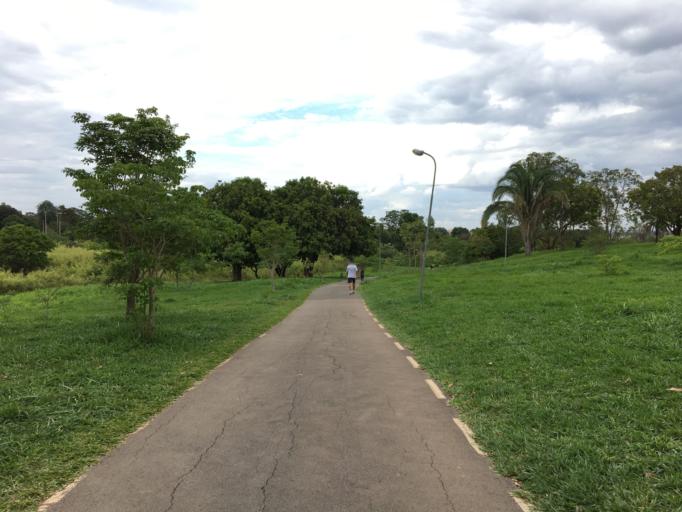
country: BR
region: Federal District
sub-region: Brasilia
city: Brasilia
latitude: -15.8325
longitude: -48.0204
